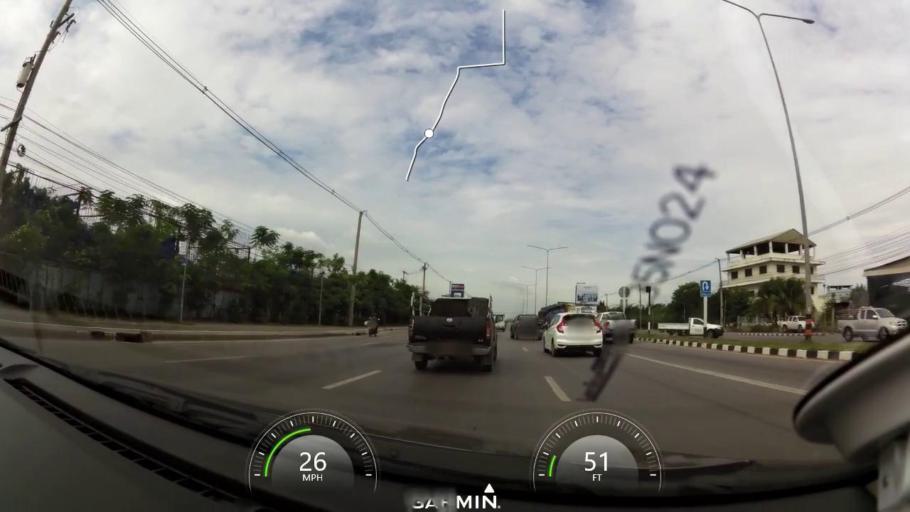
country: TH
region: Samut Sakhon
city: Krathum Baen
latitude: 13.6582
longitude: 100.3098
